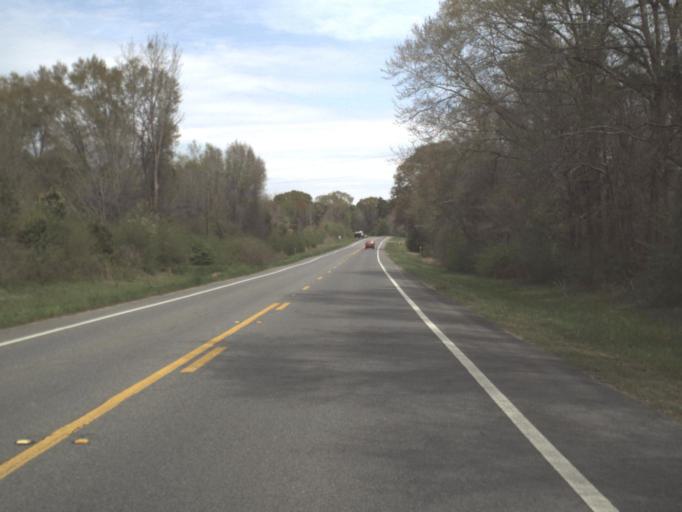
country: US
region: Florida
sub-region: Washington County
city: Chipley
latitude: 30.8581
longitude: -85.4970
